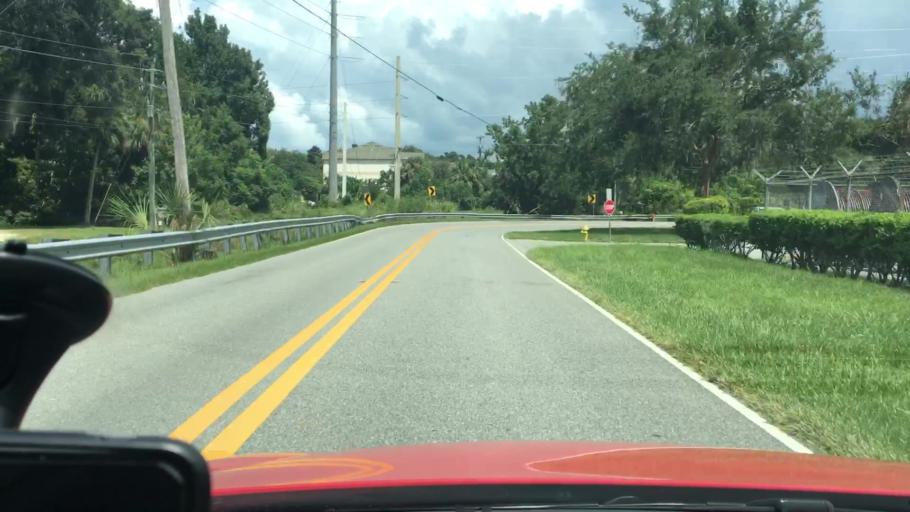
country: US
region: Florida
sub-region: Volusia County
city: Port Orange
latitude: 29.1407
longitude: -80.9991
